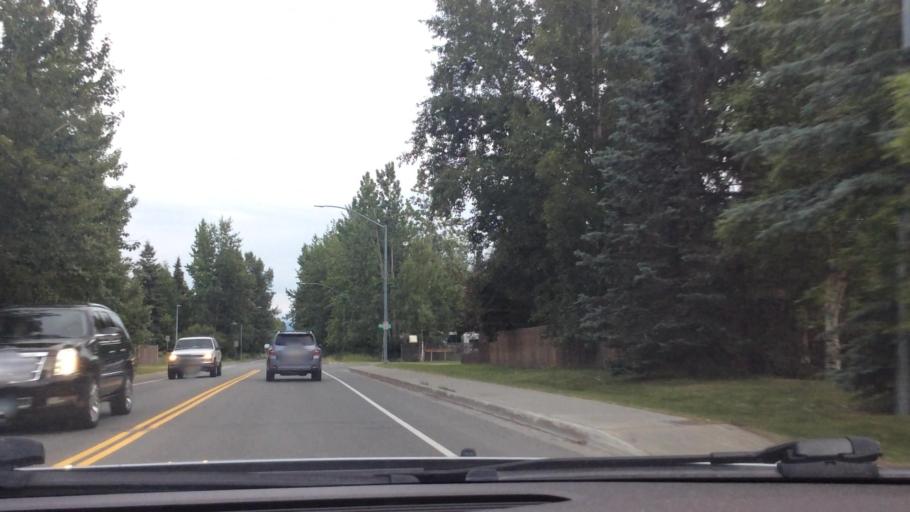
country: US
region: Alaska
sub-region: Anchorage Municipality
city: Anchorage
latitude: 61.1999
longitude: -149.7635
